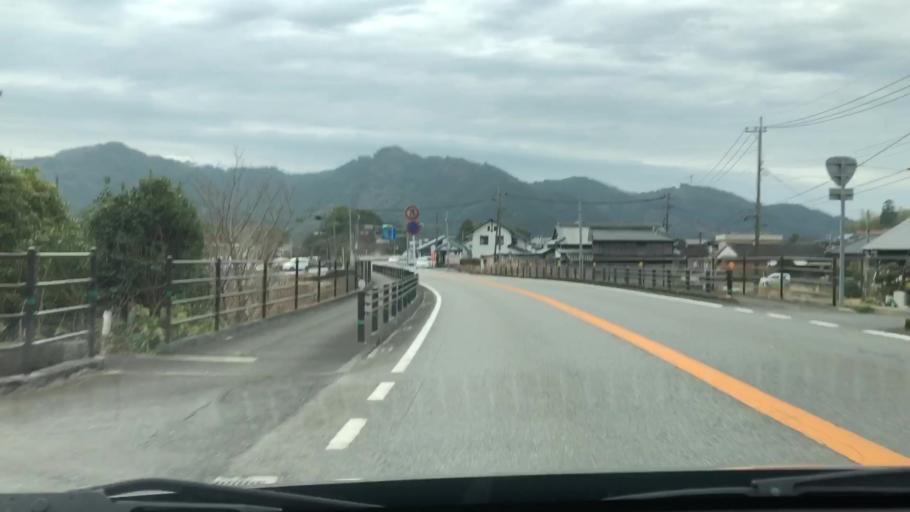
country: JP
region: Oita
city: Saiki
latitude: 32.9833
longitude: 131.8479
